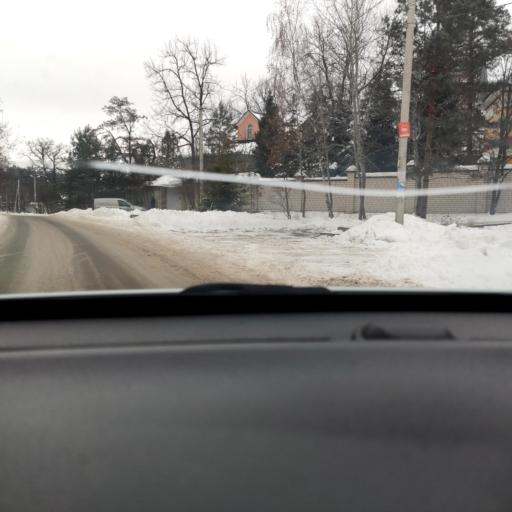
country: RU
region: Voronezj
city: Somovo
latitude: 51.7488
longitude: 39.3794
